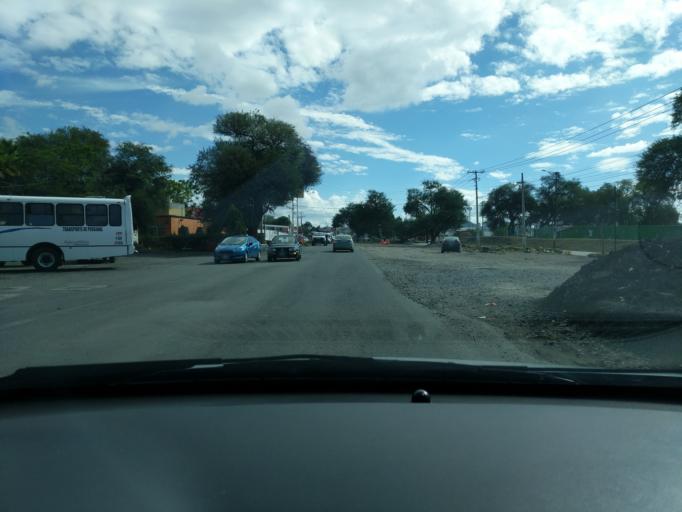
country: MX
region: Queretaro
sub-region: El Marques
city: General Lazaro Cardenas (El Colorado)
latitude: 20.5823
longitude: -100.2526
